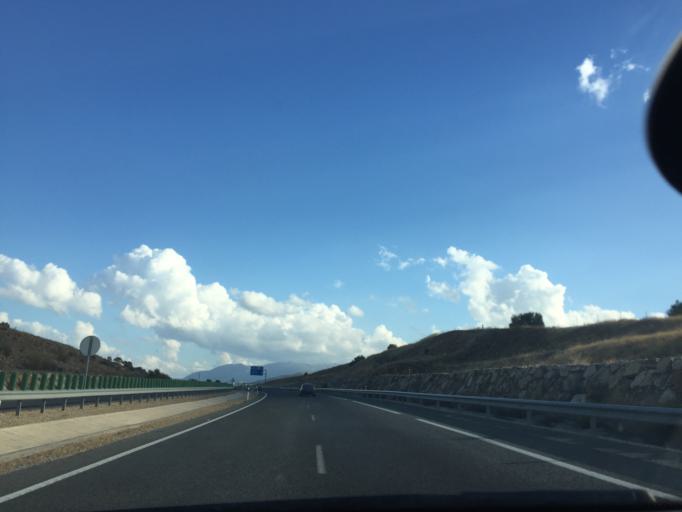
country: ES
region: Andalusia
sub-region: Provincia de Jaen
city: Jaen
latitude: 37.8091
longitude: -3.7344
